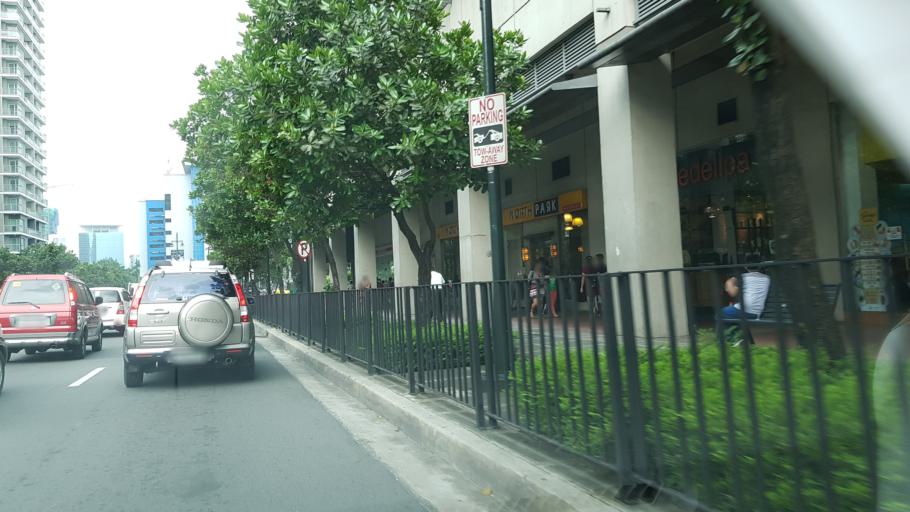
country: PH
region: Calabarzon
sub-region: Province of Rizal
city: Pateros
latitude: 14.5505
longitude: 121.0555
